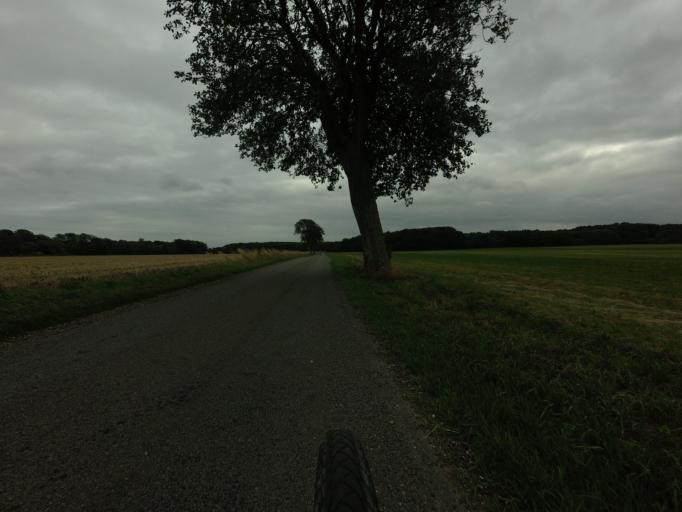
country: DK
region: Zealand
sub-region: Stevns Kommune
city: Store Heddinge
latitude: 55.3226
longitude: 12.3330
